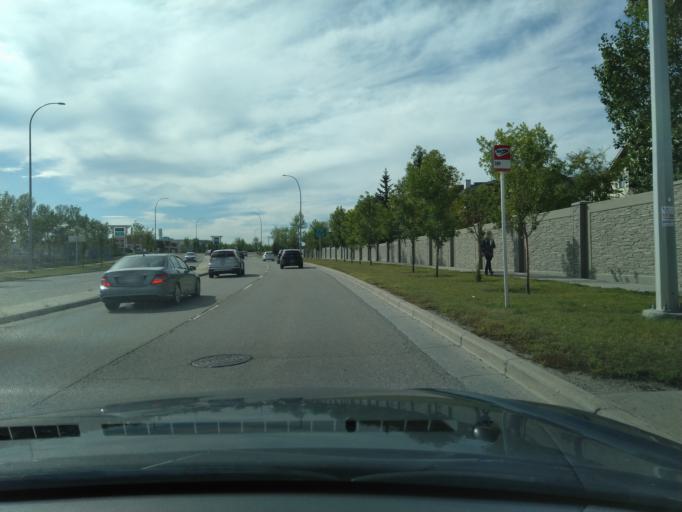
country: CA
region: Alberta
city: Calgary
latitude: 51.1418
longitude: -114.0638
